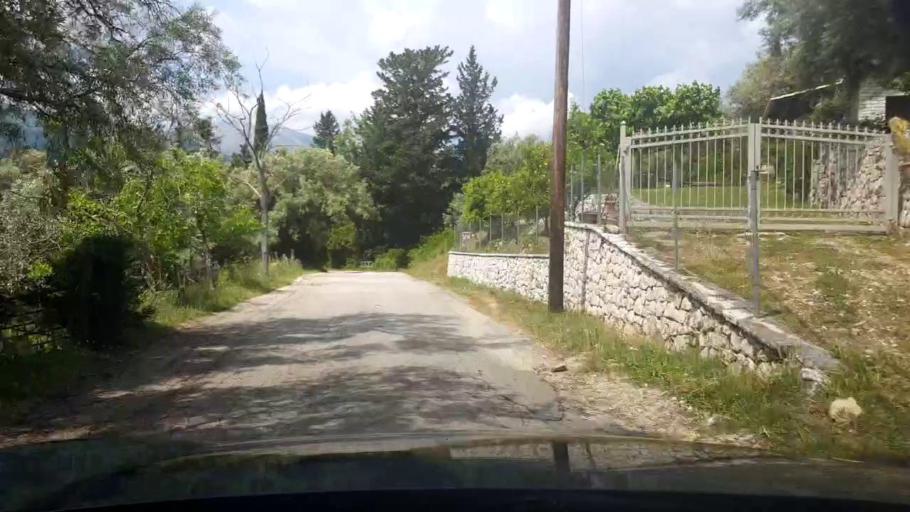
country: GR
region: Ionian Islands
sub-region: Lefkada
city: Nidri
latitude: 38.6441
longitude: 20.7059
